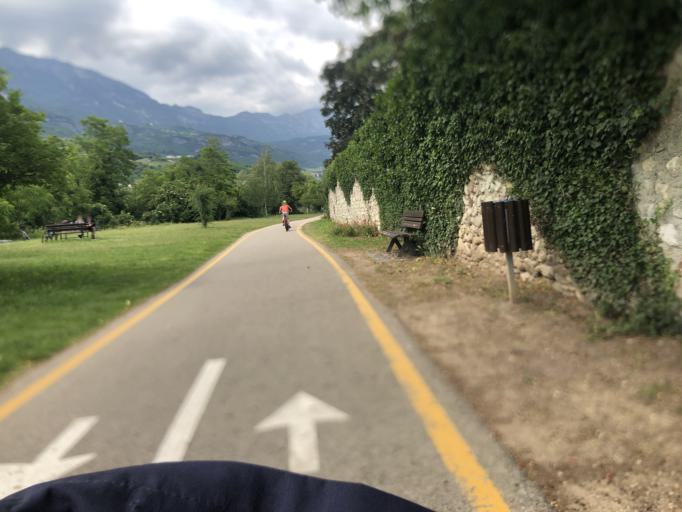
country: IT
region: Trentino-Alto Adige
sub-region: Provincia di Trento
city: Isera
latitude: 45.8894
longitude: 11.0163
